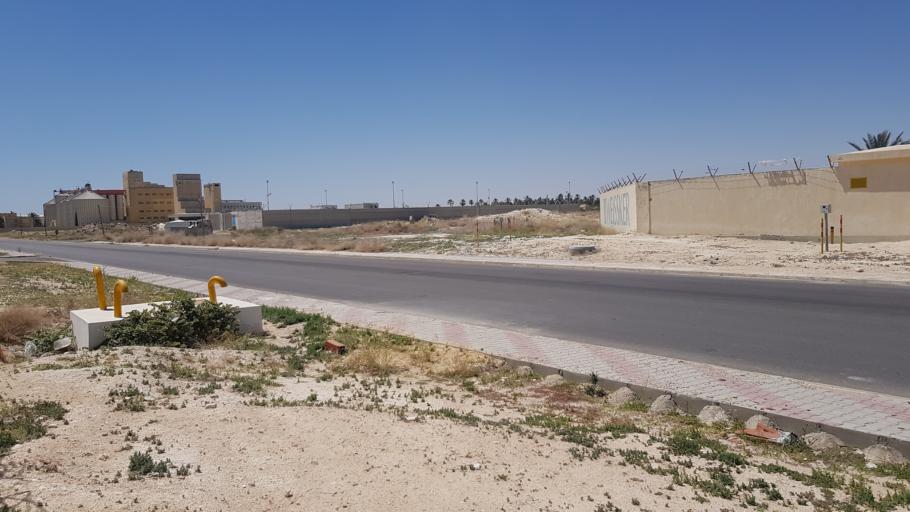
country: TN
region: Qabis
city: Gabes
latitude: 33.9129
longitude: 10.0763
